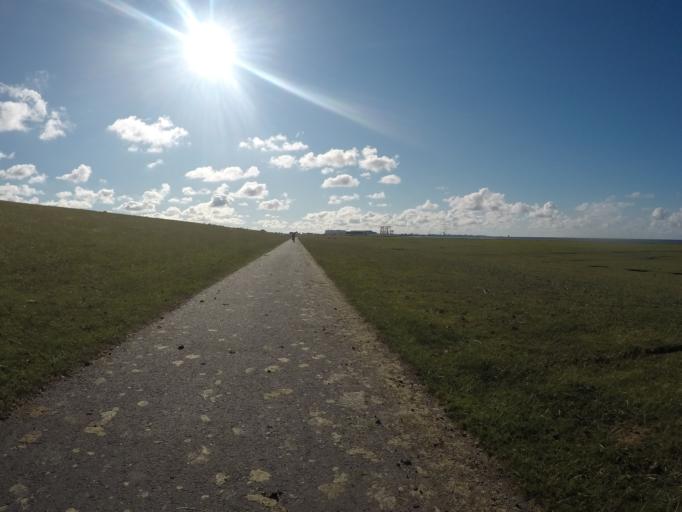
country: DE
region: Lower Saxony
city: Nordleda
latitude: 53.8326
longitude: 8.7917
